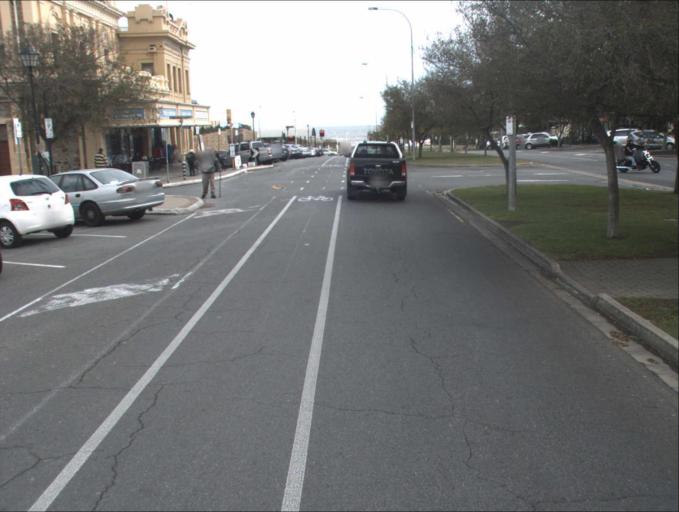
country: AU
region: South Australia
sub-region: Port Adelaide Enfield
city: Birkenhead
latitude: -34.8386
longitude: 138.4819
